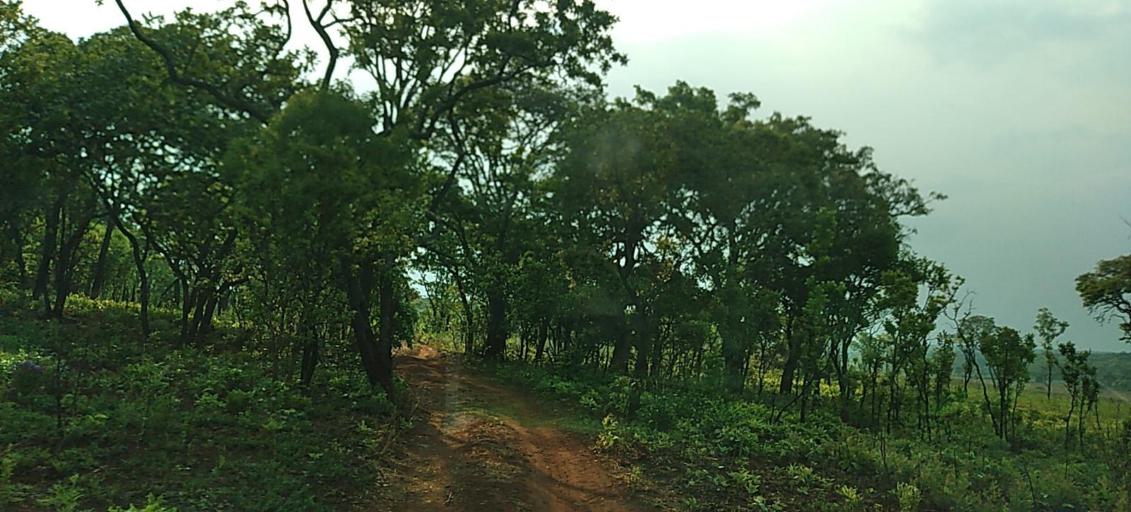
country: ZM
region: North-Western
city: Solwezi
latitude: -12.0433
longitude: 26.0520
